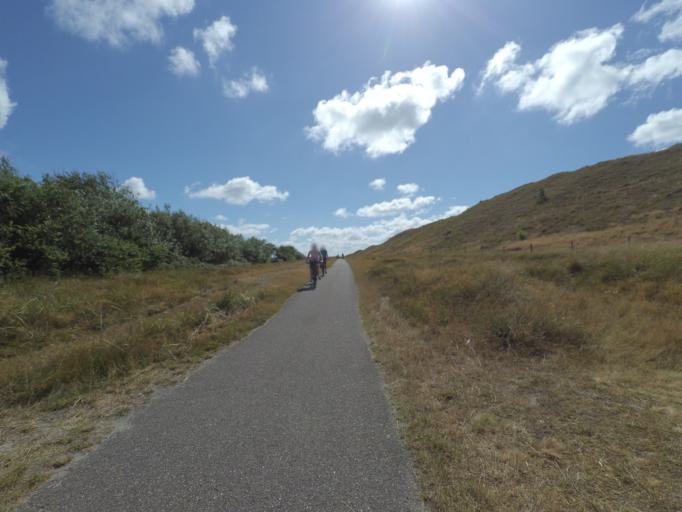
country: NL
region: North Holland
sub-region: Gemeente Texel
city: Den Burg
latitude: 53.1254
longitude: 4.8100
